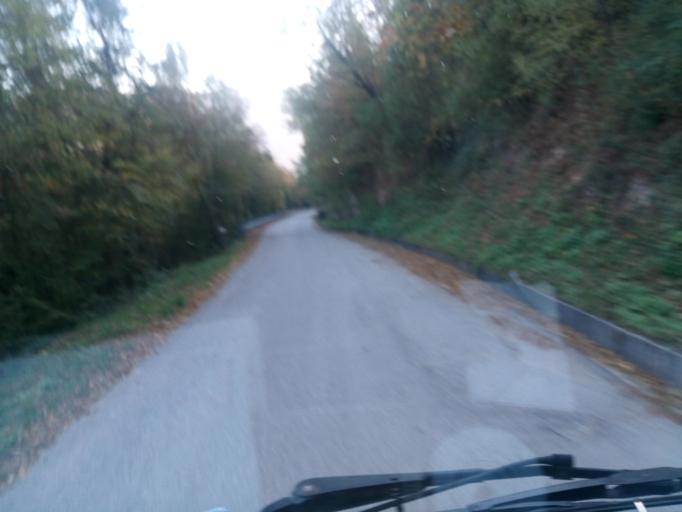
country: IT
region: Friuli Venezia Giulia
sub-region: Provincia di Udine
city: Merso di Sopra
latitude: 46.1254
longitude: 13.5188
